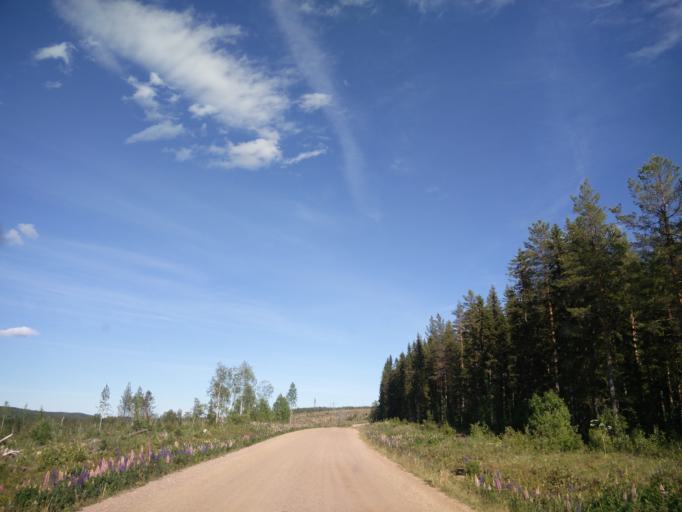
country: SE
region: Gaevleborg
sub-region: Hudiksvalls Kommun
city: Delsbo
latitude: 62.1773
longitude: 16.4997
